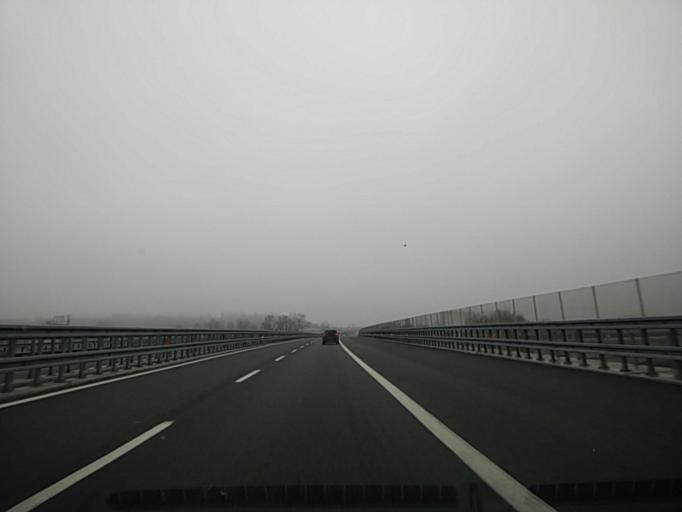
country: IT
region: Piedmont
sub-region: Provincia di Asti
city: Asti
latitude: 44.9138
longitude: 8.2274
